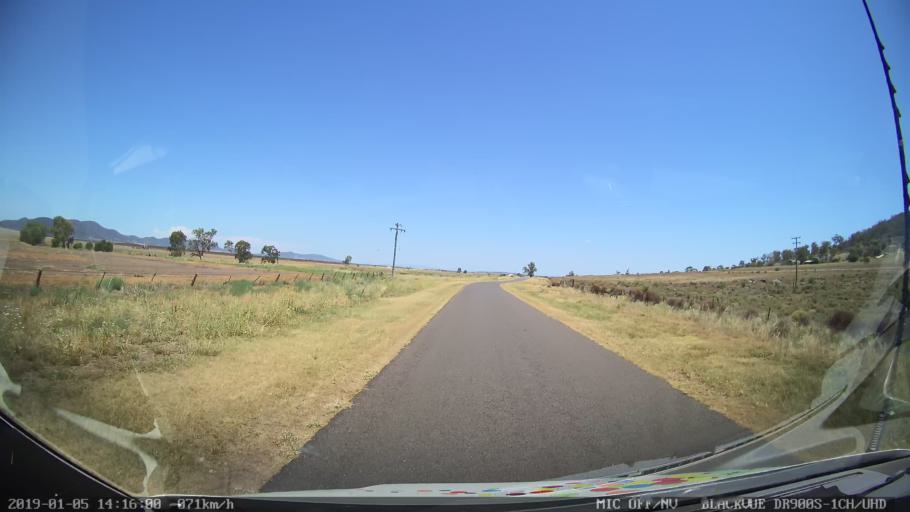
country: AU
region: New South Wales
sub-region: Liverpool Plains
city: Quirindi
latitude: -31.2525
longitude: 150.4721
